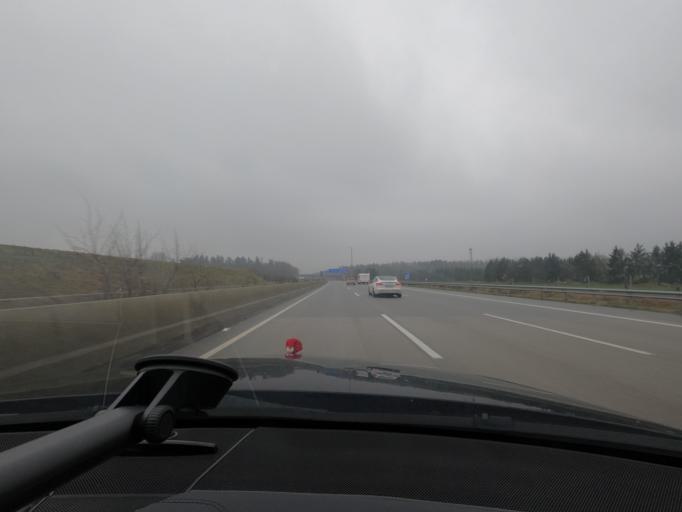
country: DE
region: Schleswig-Holstein
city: Bimohlen
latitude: 53.9078
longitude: 9.9365
